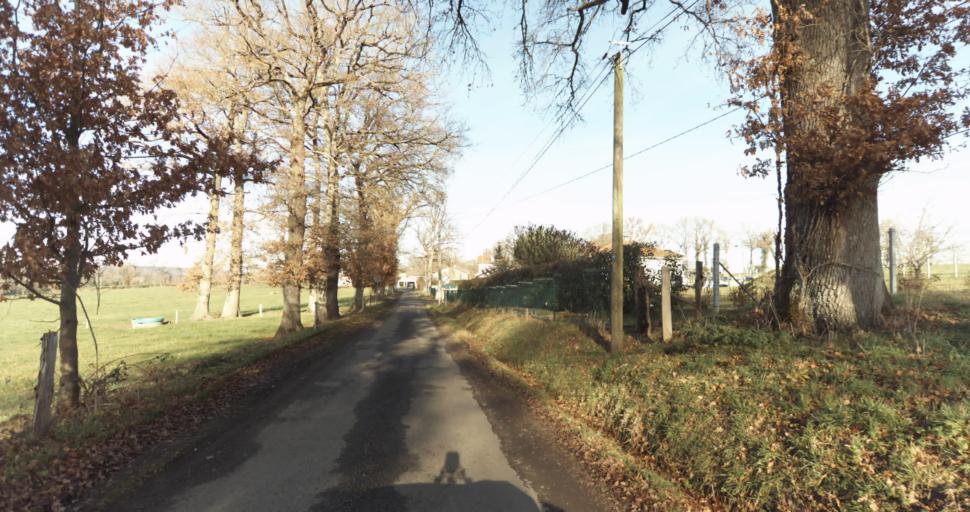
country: FR
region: Limousin
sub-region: Departement de la Haute-Vienne
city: Aixe-sur-Vienne
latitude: 45.7839
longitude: 1.1162
